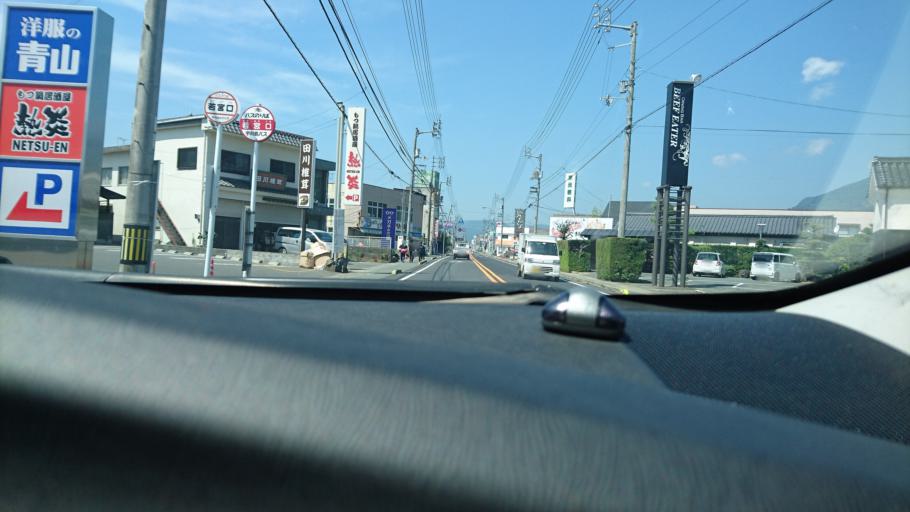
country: JP
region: Ehime
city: Ozu
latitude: 33.5233
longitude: 132.5573
